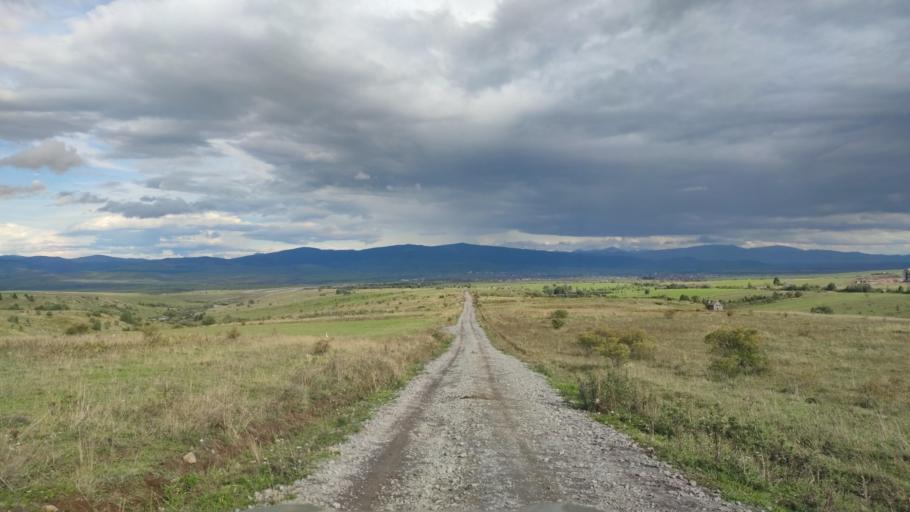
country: RO
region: Harghita
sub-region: Comuna Remetea
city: Remetea
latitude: 46.8164
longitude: 25.3701
